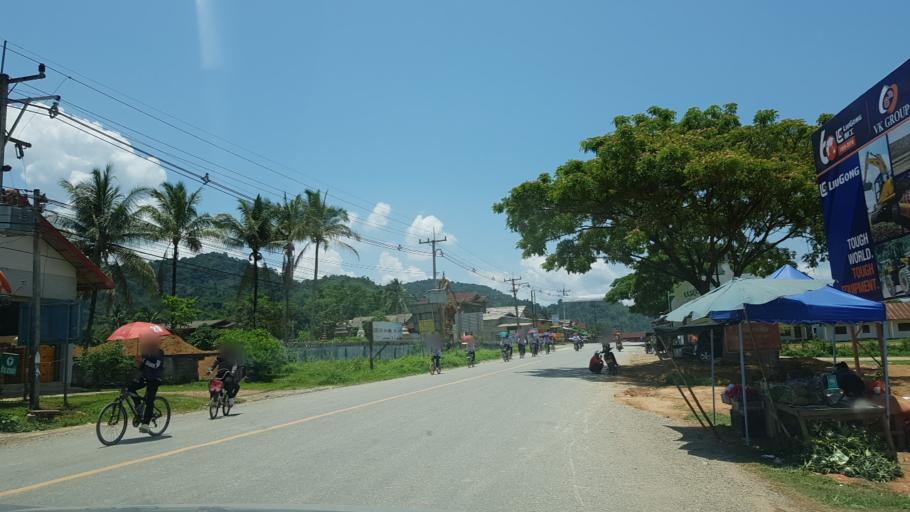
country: LA
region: Vientiane
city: Muang Kasi
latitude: 19.2256
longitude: 102.2524
